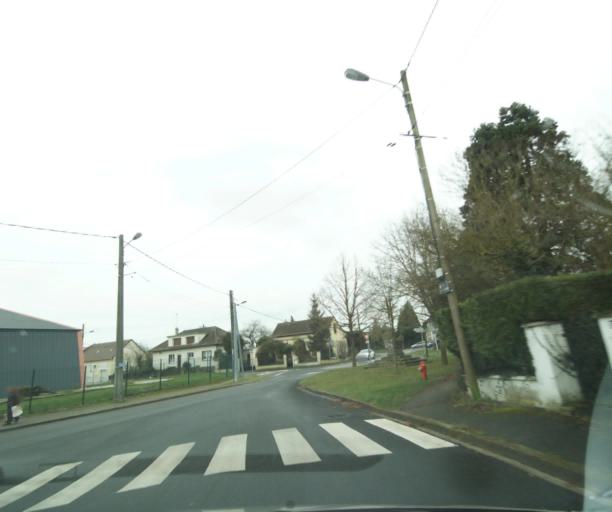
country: FR
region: Picardie
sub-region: Departement de l'Oise
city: Noyon
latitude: 49.5746
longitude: 2.9941
